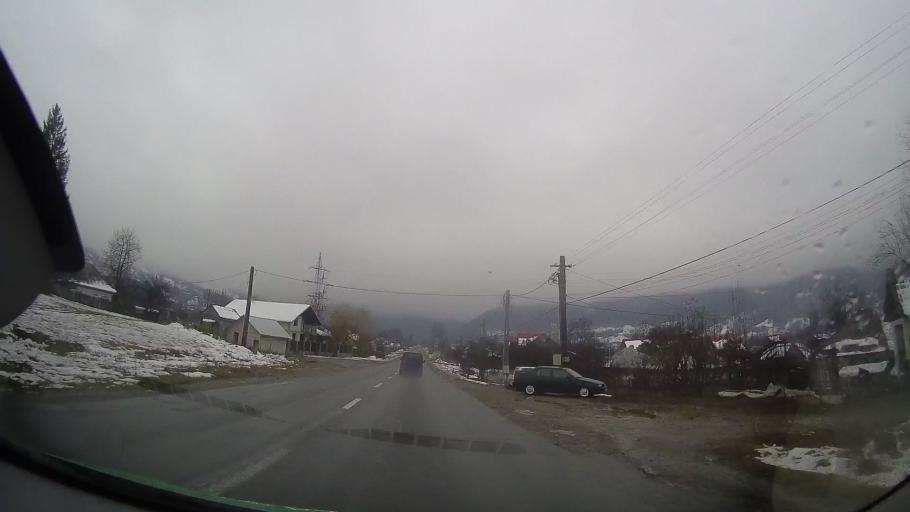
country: RO
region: Neamt
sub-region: Comuna Pangarati
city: Stejaru
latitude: 46.9096
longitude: 26.1785
